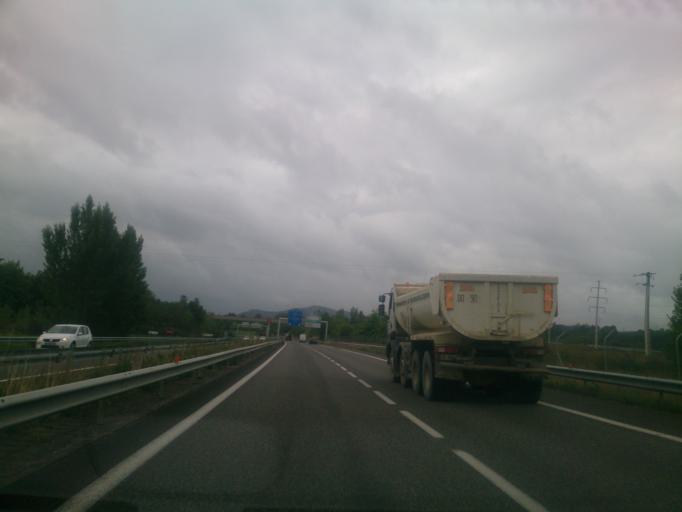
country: FR
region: Midi-Pyrenees
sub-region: Departement de la Haute-Garonne
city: Martres-Tolosane
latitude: 43.1907
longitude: 0.9842
